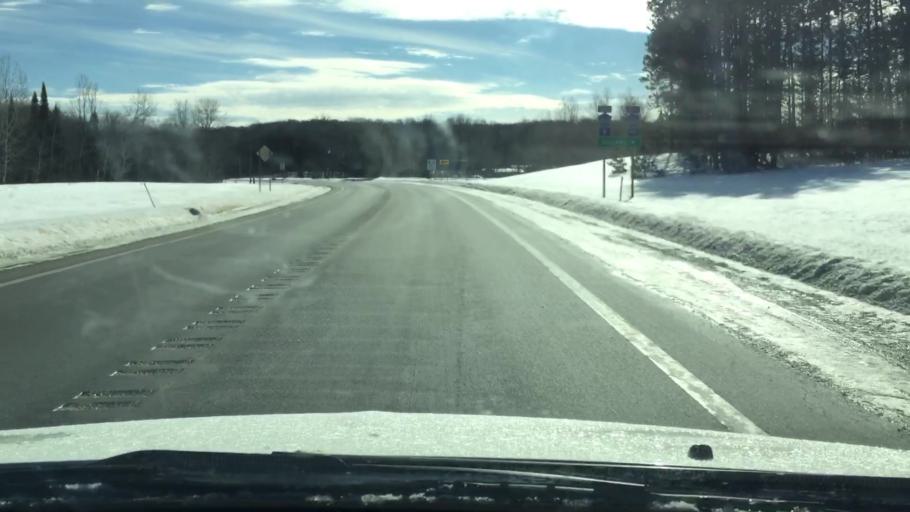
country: US
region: Michigan
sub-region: Antrim County
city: Mancelona
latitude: 44.9944
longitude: -85.0619
